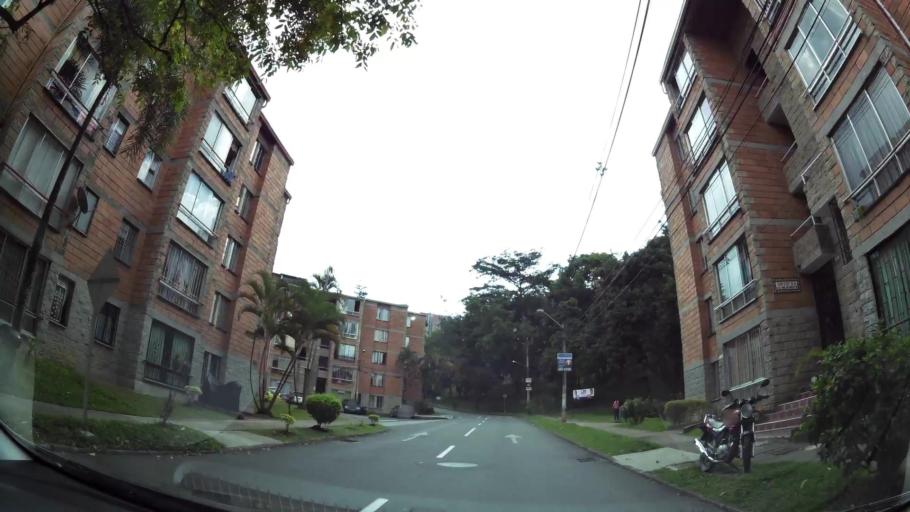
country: CO
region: Antioquia
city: Envigado
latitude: 6.1600
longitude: -75.5970
